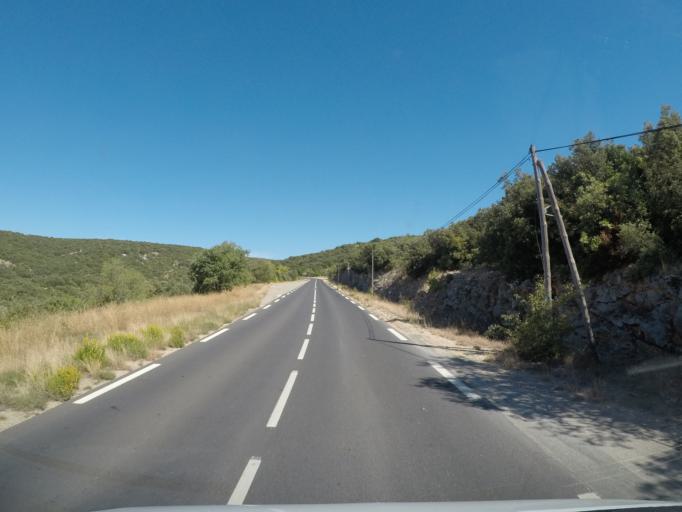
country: FR
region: Languedoc-Roussillon
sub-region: Departement de l'Herault
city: Aniane
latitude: 43.7220
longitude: 3.6265
